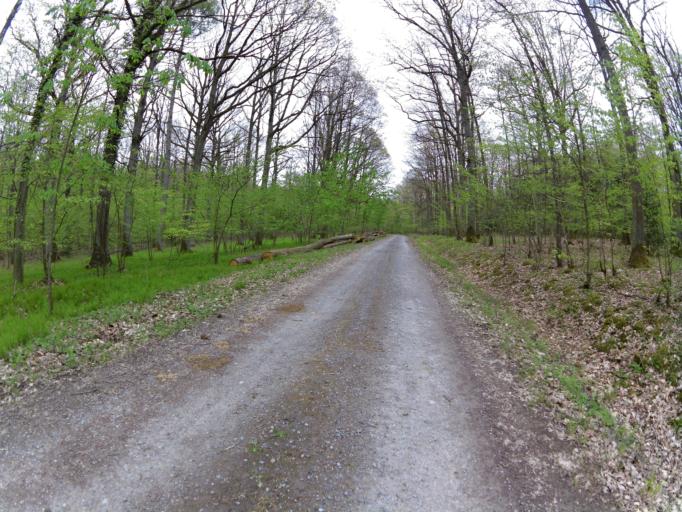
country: DE
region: Bavaria
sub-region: Regierungsbezirk Unterfranken
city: Prosselsheim
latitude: 49.8558
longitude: 10.1518
